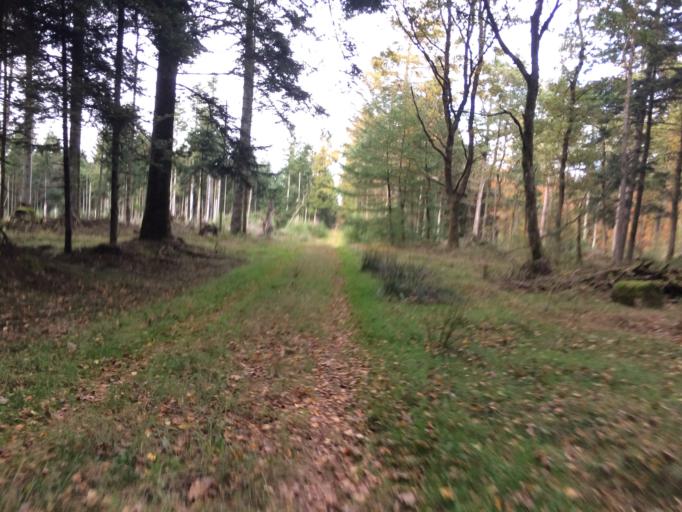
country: DK
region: Central Jutland
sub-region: Holstebro Kommune
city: Ulfborg
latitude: 56.2110
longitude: 8.4443
